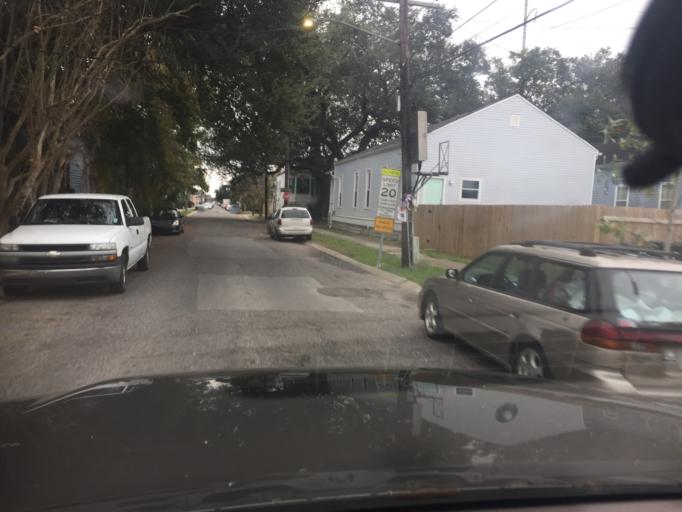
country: US
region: Louisiana
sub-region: Orleans Parish
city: New Orleans
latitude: 29.9739
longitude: -90.0785
